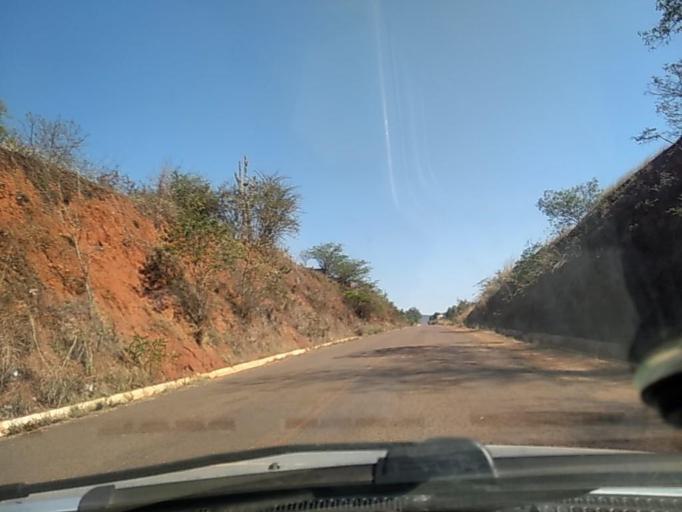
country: BR
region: Bahia
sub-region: Caetite
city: Caetite
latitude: -14.0460
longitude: -42.4855
